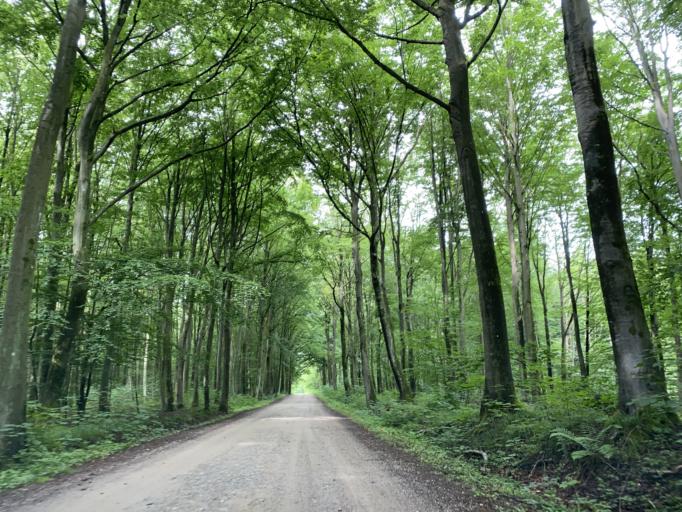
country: DK
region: South Denmark
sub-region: Sonderborg Kommune
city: Sonderborg
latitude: 54.9028
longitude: 9.8337
